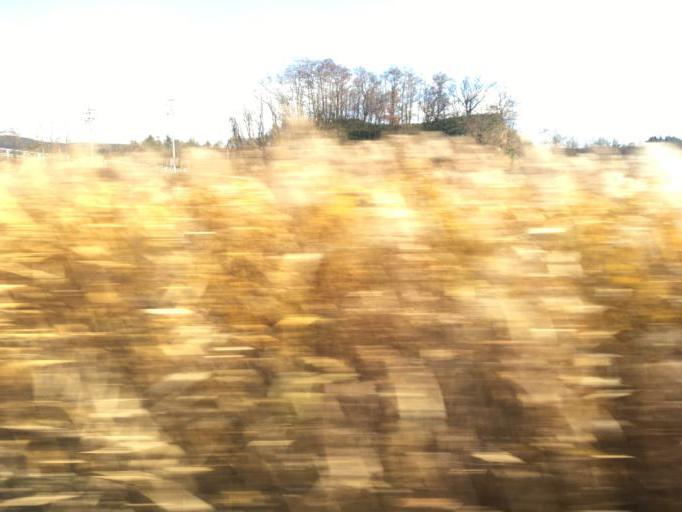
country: JP
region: Akita
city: Yokotemachi
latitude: 39.2693
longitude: 140.5485
